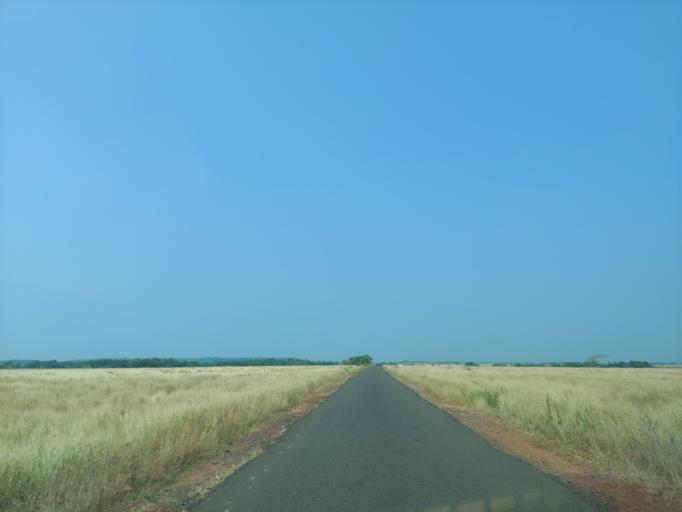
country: IN
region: Maharashtra
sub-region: Sindhudurg
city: Malvan
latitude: 15.9946
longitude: 73.5221
